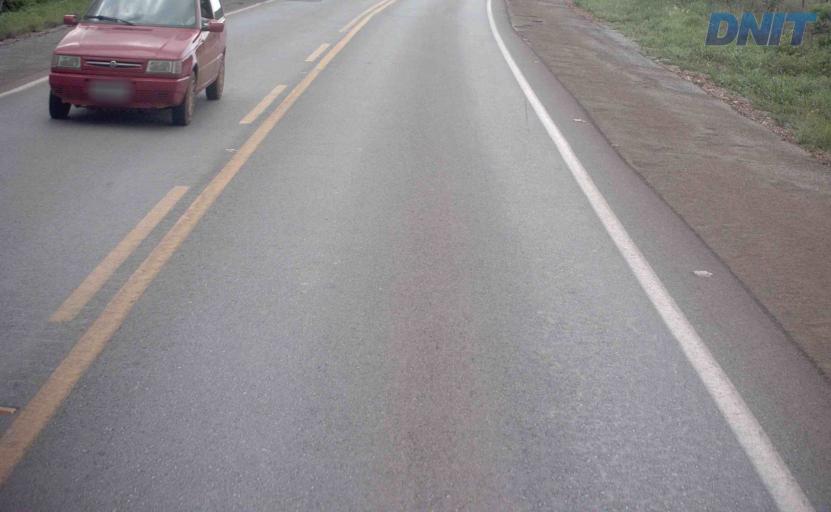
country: BR
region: Goias
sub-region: Barro Alto
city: Barro Alto
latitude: -14.8970
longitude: -48.9677
